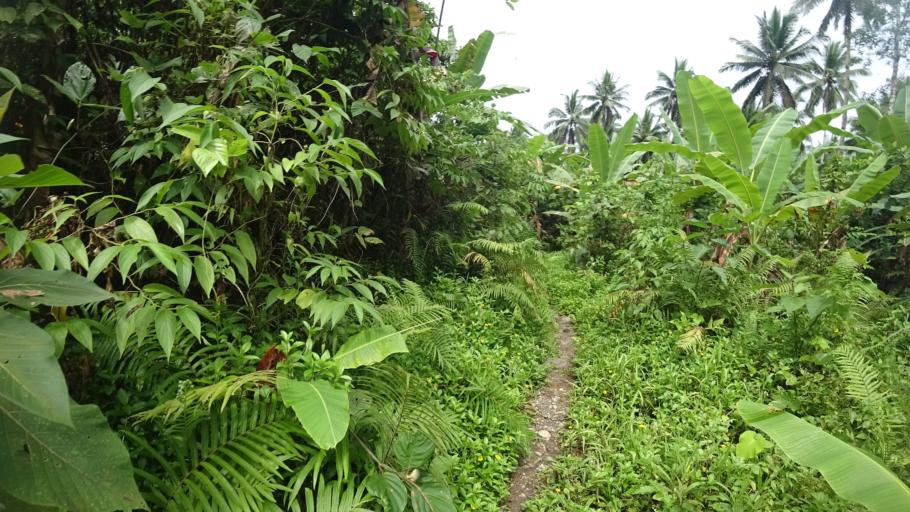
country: PH
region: Eastern Visayas
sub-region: Province of Leyte
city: Bugho
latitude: 10.8264
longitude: 124.8812
